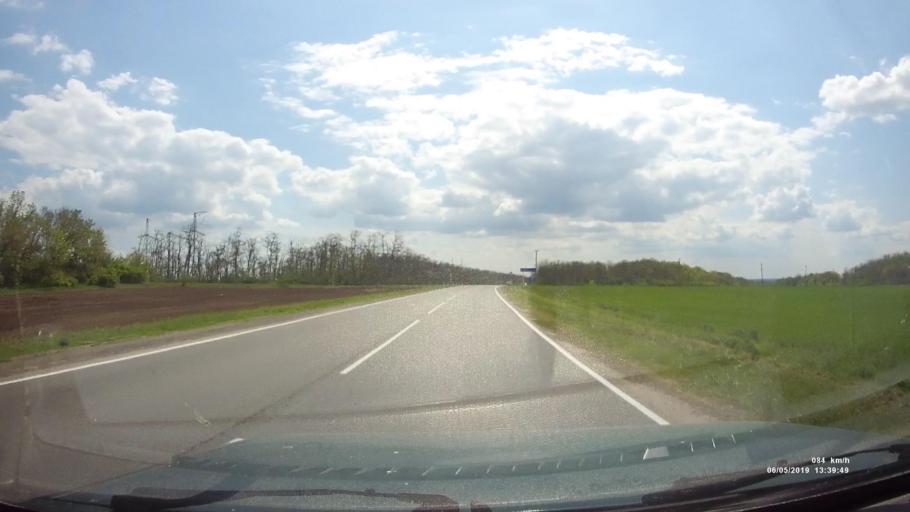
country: RU
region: Rostov
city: Ust'-Donetskiy
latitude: 47.6713
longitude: 40.7014
